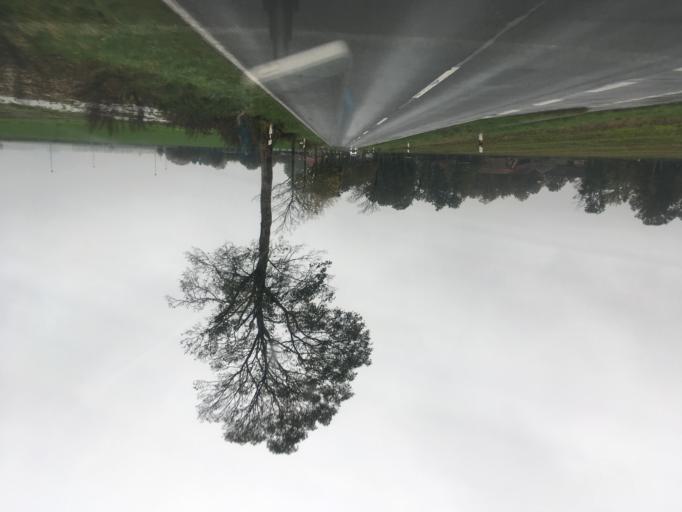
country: DE
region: Lower Saxony
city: Bergen
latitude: 52.8165
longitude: 10.0048
